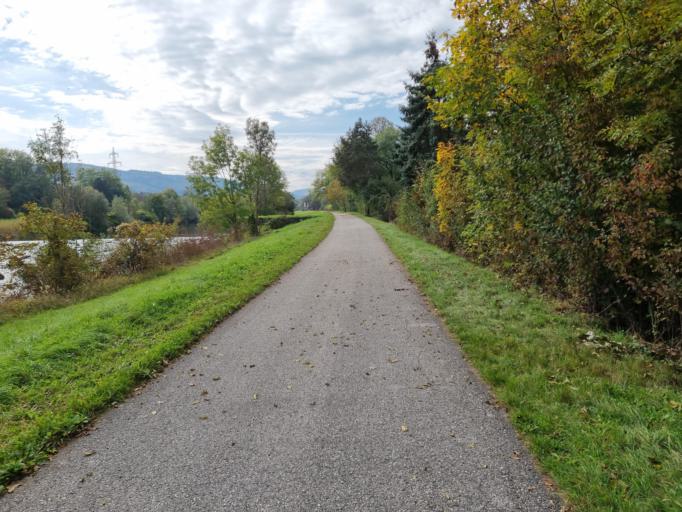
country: AT
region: Lower Austria
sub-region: Politischer Bezirk Sankt Polten
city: Wilhelmsburg
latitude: 48.1360
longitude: 15.6327
